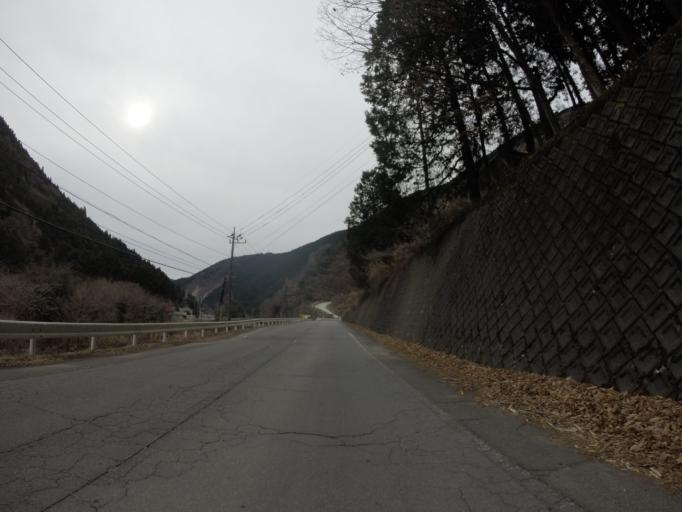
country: JP
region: Shizuoka
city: Fujinomiya
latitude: 35.2485
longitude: 138.5293
